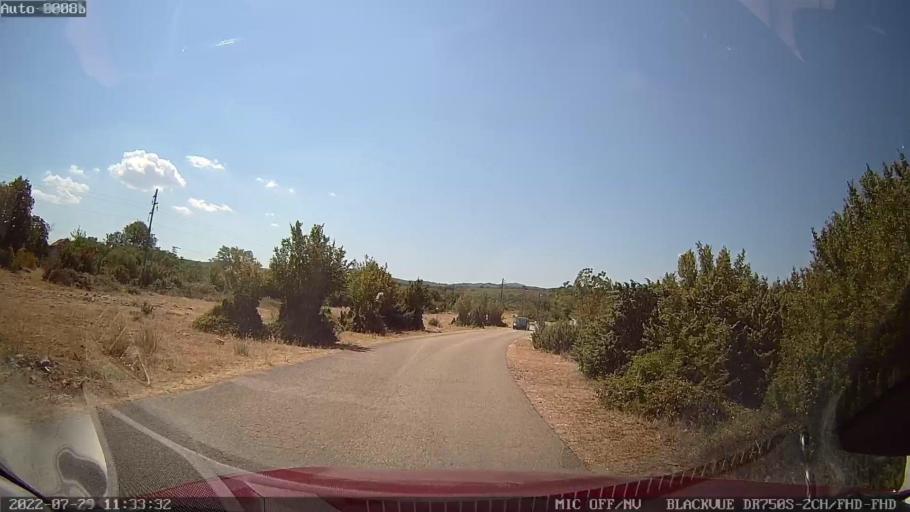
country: HR
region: Zadarska
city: Obrovac
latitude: 44.1850
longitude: 15.7325
